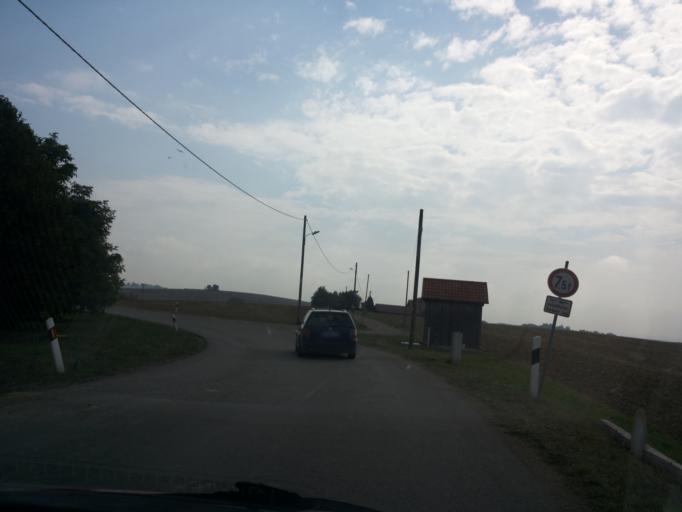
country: DE
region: Bavaria
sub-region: Upper Bavaria
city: Oberdolling
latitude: 48.7951
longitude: 11.5791
